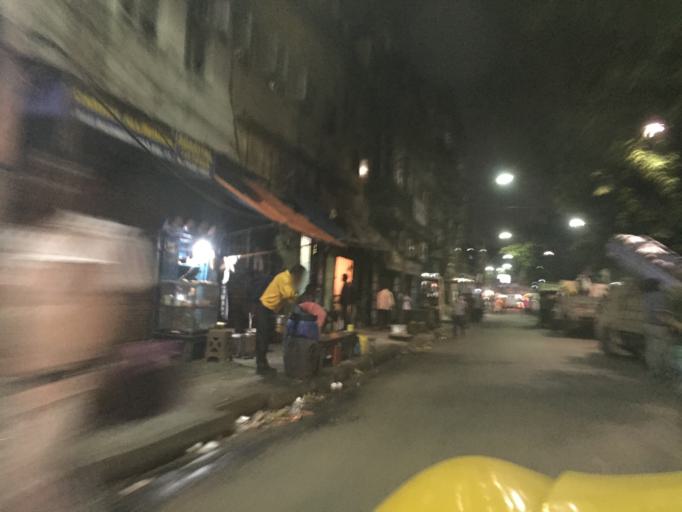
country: IN
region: West Bengal
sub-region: Kolkata
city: Bara Bazar
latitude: 22.5634
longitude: 88.3560
